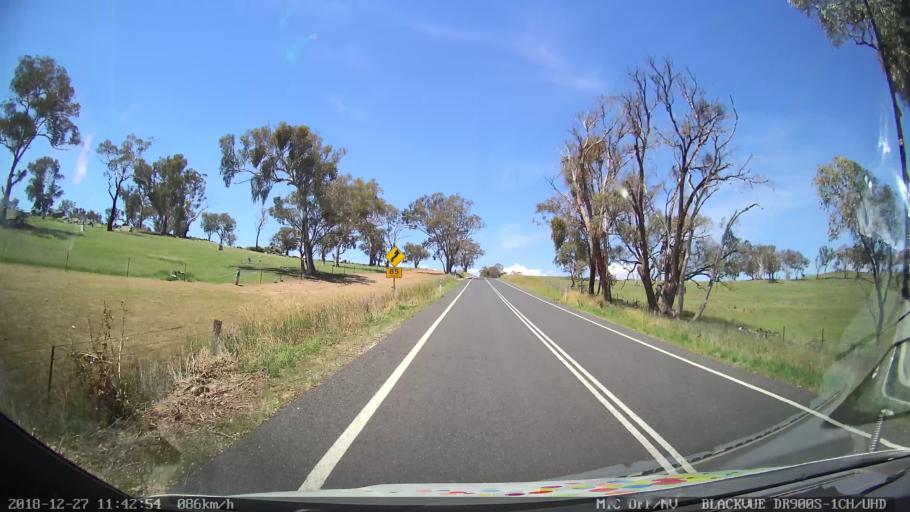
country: AU
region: New South Wales
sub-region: Bathurst Regional
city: Perthville
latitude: -33.5542
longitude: 149.4770
